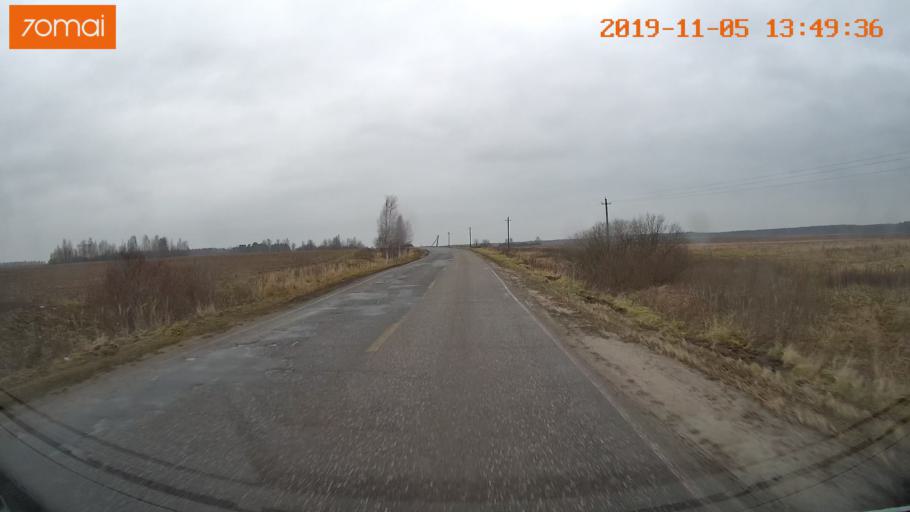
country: RU
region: Ivanovo
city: Kaminskiy
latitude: 57.0122
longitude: 41.4103
